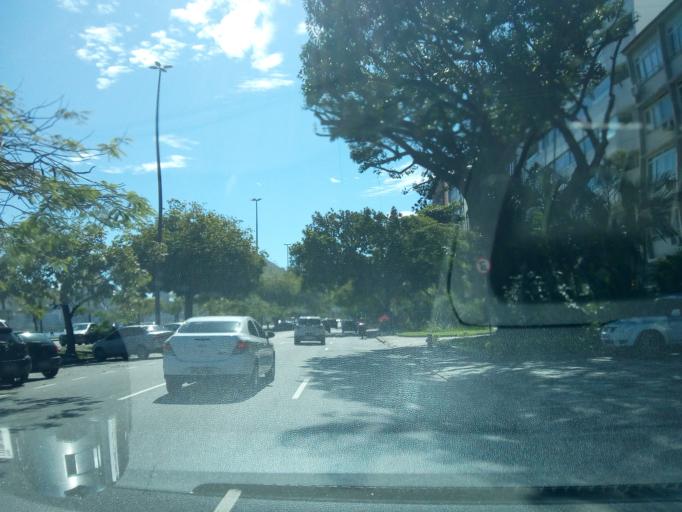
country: BR
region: Rio de Janeiro
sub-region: Rio De Janeiro
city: Rio de Janeiro
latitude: -22.9806
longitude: -43.2126
